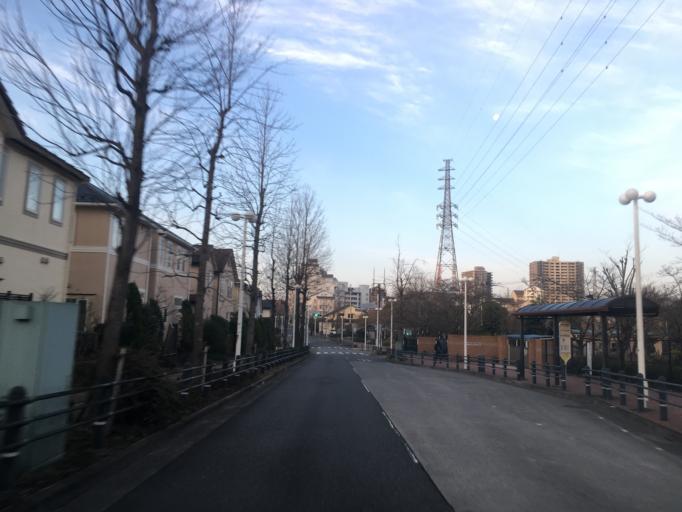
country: JP
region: Tokyo
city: Hino
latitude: 35.6178
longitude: 139.3925
